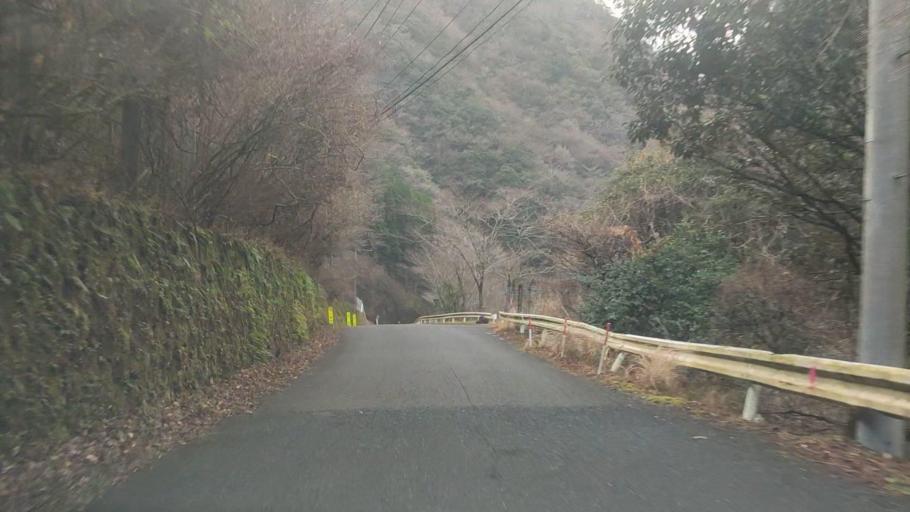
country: JP
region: Kumamoto
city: Matsubase
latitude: 32.4851
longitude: 130.8942
